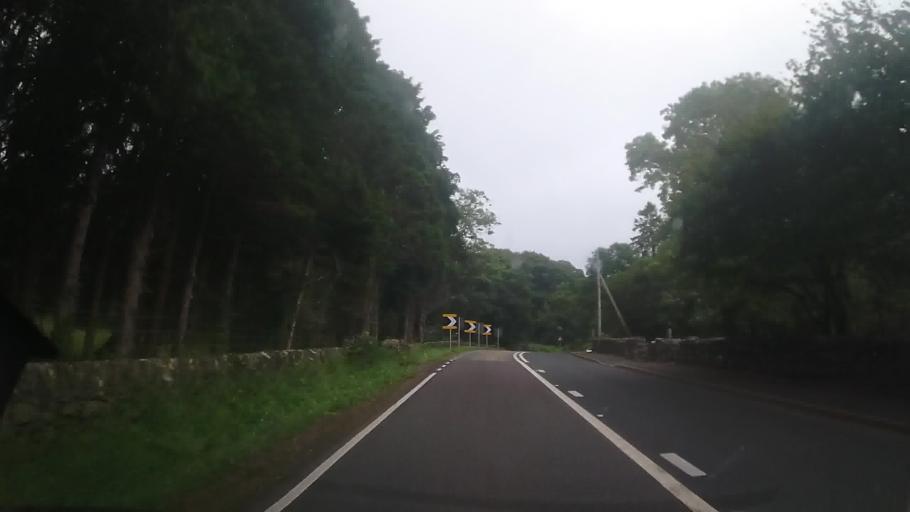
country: GB
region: Wales
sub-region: Conwy
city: Betws-y-Coed
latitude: 53.0999
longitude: -3.8720
